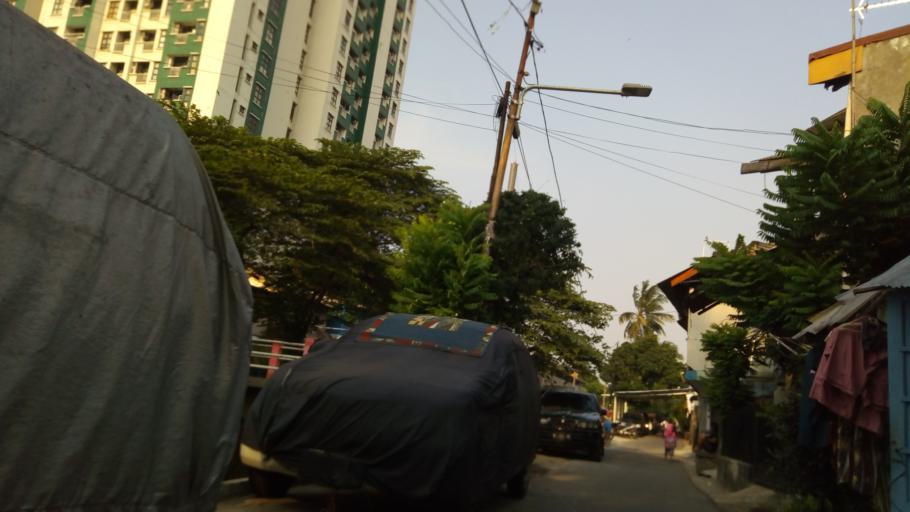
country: ID
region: Jakarta Raya
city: Jakarta
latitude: -6.1957
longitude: 106.8549
